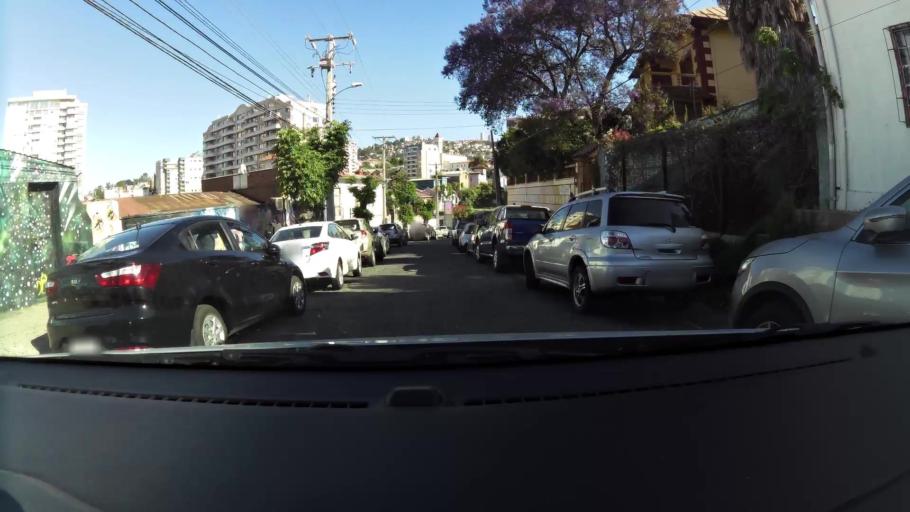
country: CL
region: Valparaiso
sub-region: Provincia de Valparaiso
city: Vina del Mar
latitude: -33.0257
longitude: -71.5633
